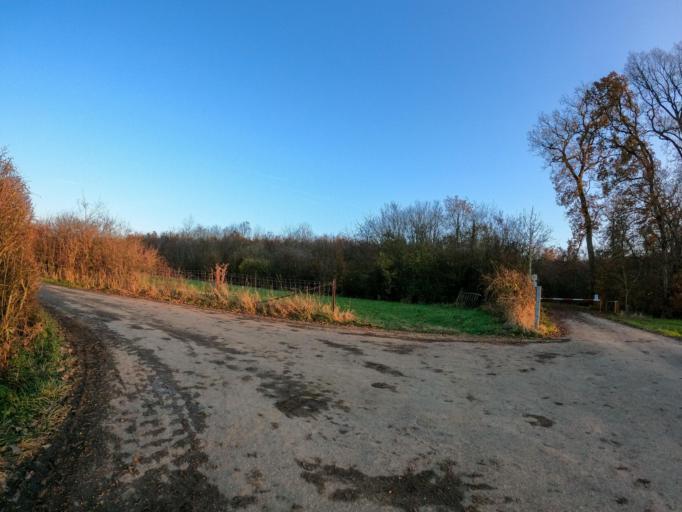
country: LU
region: Luxembourg
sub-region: Canton de Luxembourg
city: Bertrange
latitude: 49.5889
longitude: 6.0355
